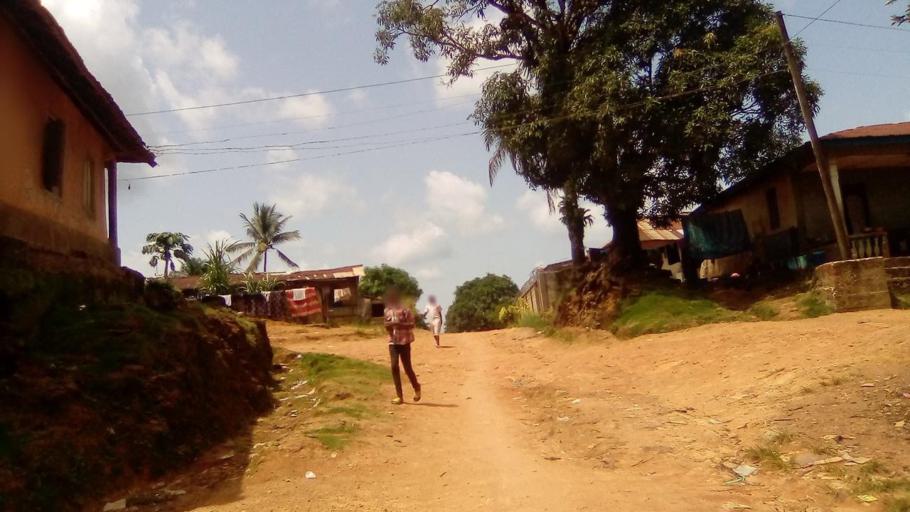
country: SL
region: Southern Province
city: Bo
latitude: 7.9658
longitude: -11.7304
